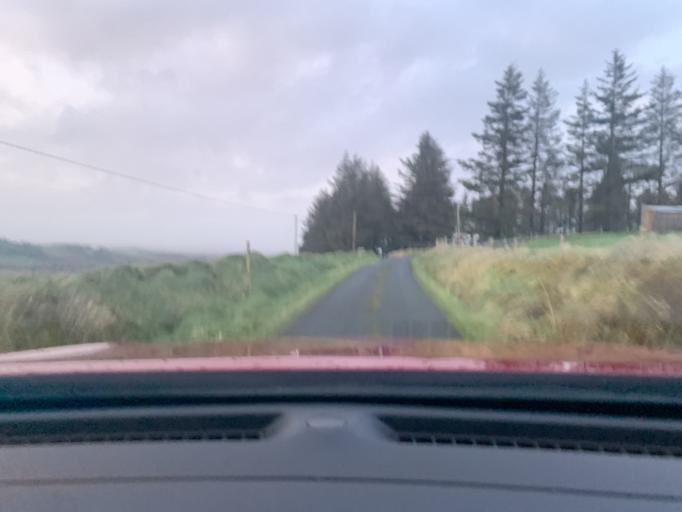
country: IE
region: Connaught
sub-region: Sligo
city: Ballymote
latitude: 54.0582
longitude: -8.3973
